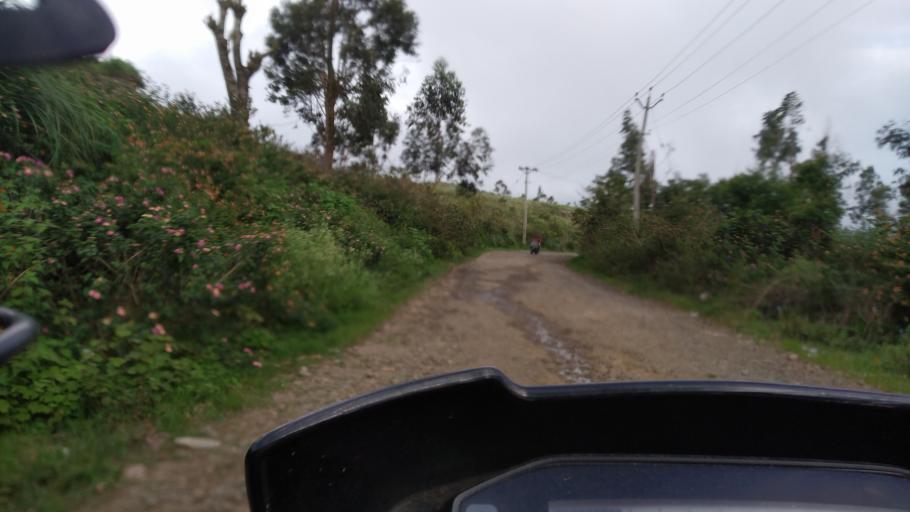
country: IN
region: Kerala
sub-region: Idukki
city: Munnar
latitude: 10.0409
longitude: 77.1792
